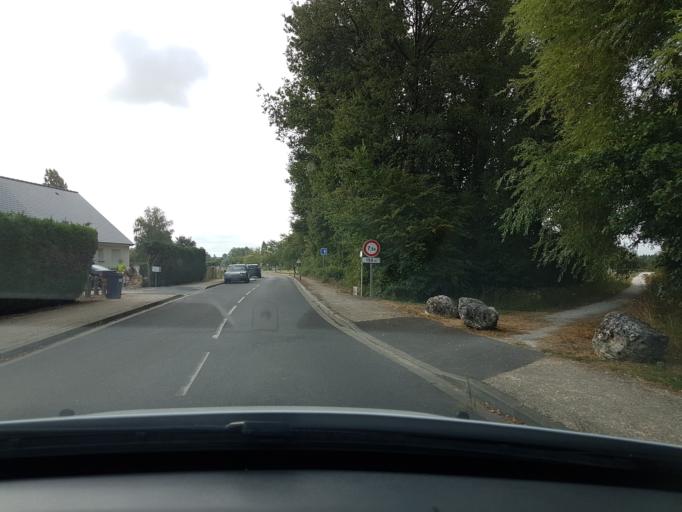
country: FR
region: Centre
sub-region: Departement d'Indre-et-Loire
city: Larcay
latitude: 47.3512
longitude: 0.7702
